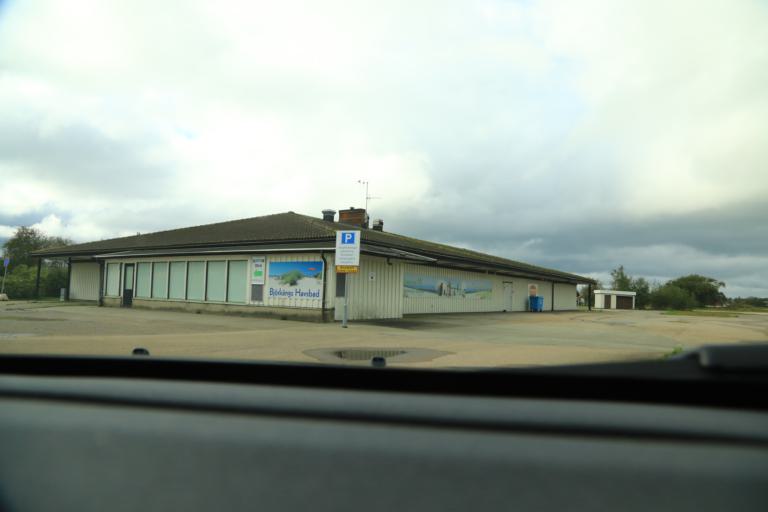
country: SE
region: Halland
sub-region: Varbergs Kommun
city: Tvaaker
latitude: 57.0120
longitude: 12.3556
